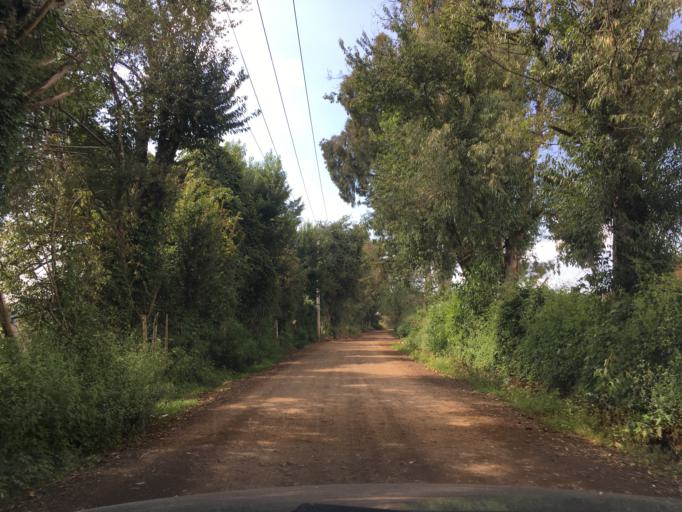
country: MX
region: Michoacan
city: Acuitzio del Canje
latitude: 19.5172
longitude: -101.2195
